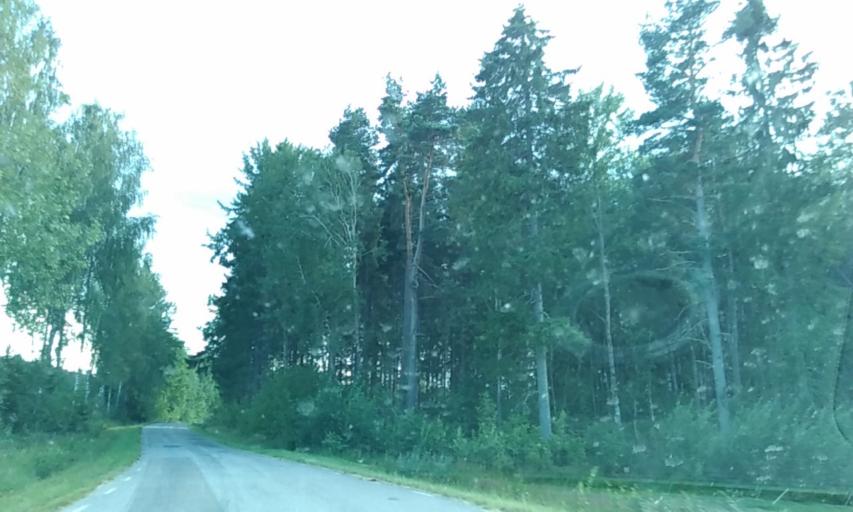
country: SE
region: Vaestra Goetaland
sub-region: Lidkopings Kommun
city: Lidkoping
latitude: 58.5570
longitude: 13.0098
